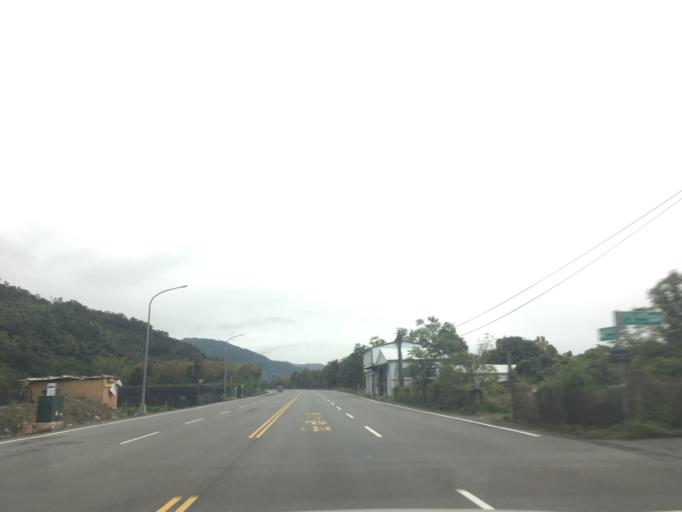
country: TW
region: Taiwan
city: Taitung City
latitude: 22.7340
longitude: 121.0564
